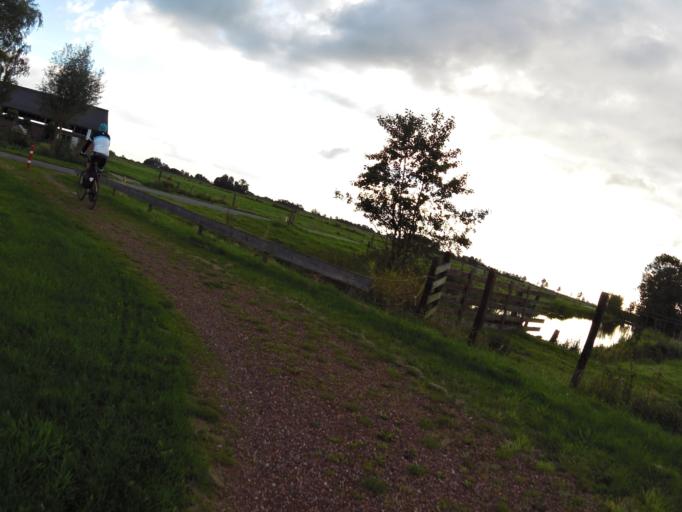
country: NL
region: Utrecht
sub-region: Gemeente Woerden
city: Woerden
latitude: 52.1383
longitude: 4.8696
